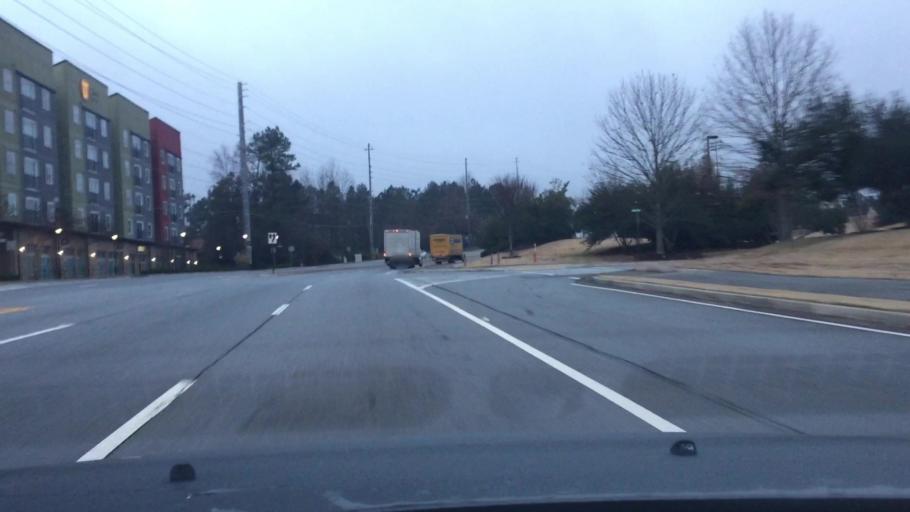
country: US
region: Georgia
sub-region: Cobb County
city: Kennesaw
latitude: 34.0281
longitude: -84.5643
